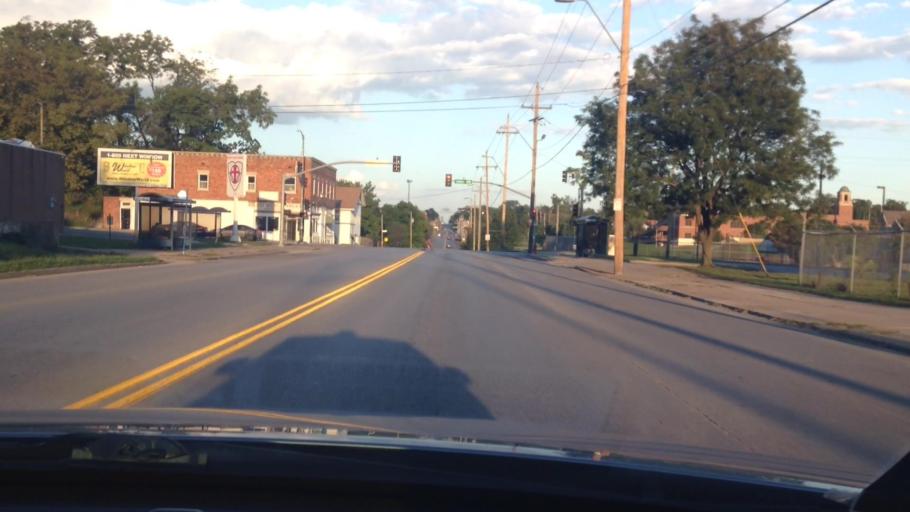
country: US
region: Missouri
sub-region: Jackson County
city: Kansas City
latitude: 39.0696
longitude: -94.5446
